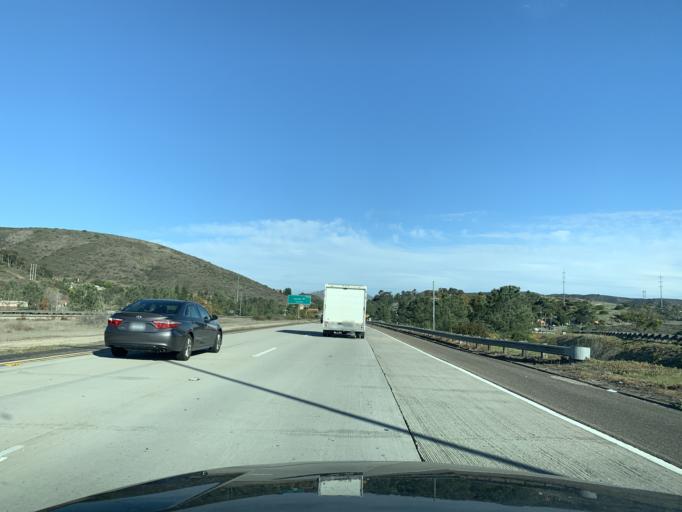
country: US
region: California
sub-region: San Diego County
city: Fairbanks Ranch
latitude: 32.9573
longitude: -117.1168
